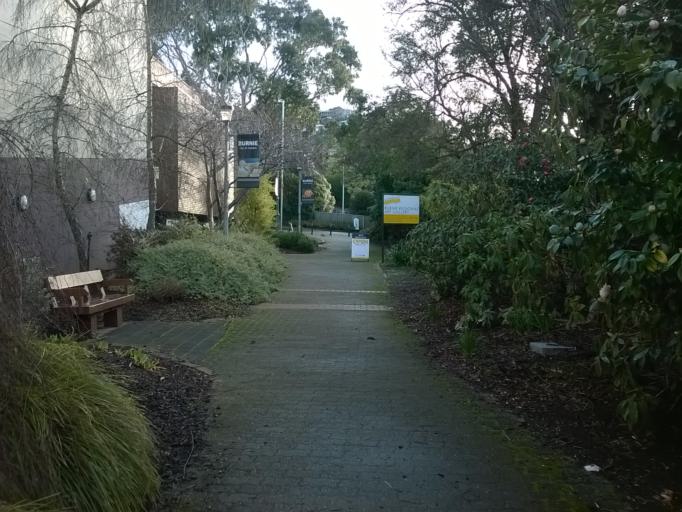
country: AU
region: Tasmania
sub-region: Burnie
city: Burnie
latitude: -41.0506
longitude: 145.9029
